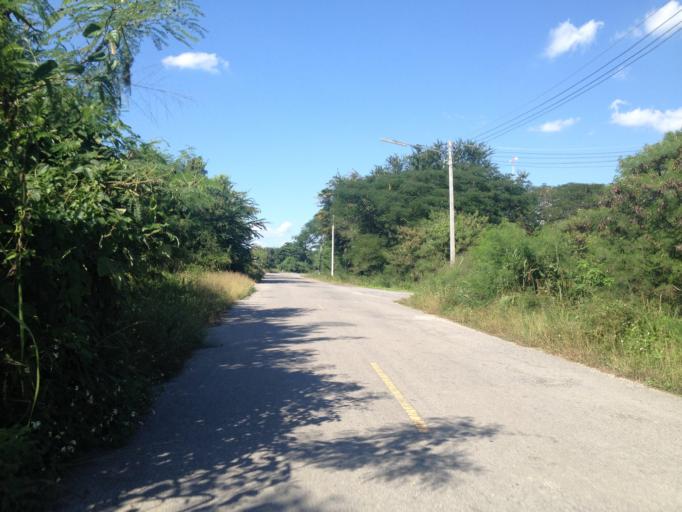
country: TH
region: Chiang Mai
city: Saraphi
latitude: 18.6875
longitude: 98.9873
